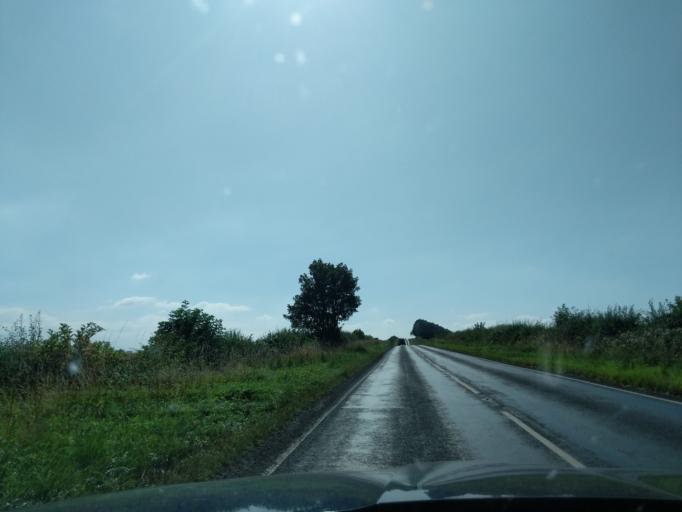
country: GB
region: England
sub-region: Northumberland
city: Ford
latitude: 55.7028
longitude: -2.1486
